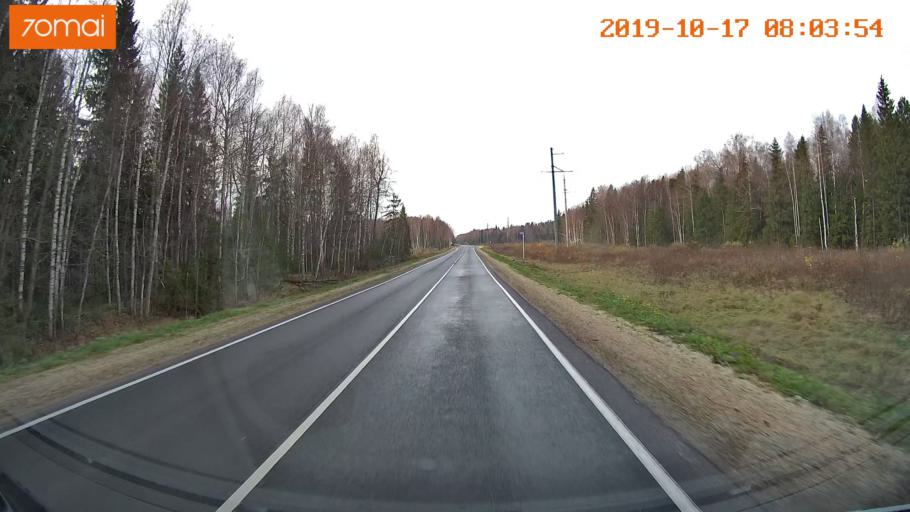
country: RU
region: Vladimir
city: Belaya Rechka
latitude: 56.3511
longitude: 39.4462
